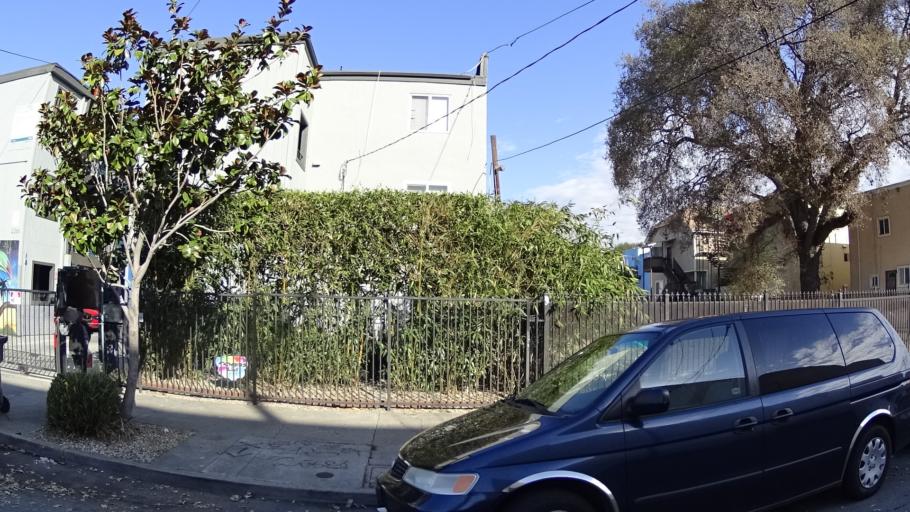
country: US
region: California
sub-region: Alameda County
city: Alameda
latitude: 37.7845
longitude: -122.2356
